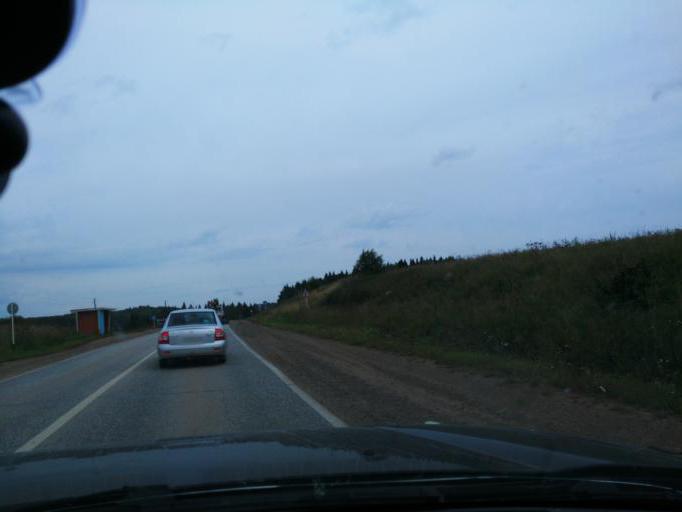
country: RU
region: Perm
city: Chernushka
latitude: 56.5656
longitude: 56.1188
